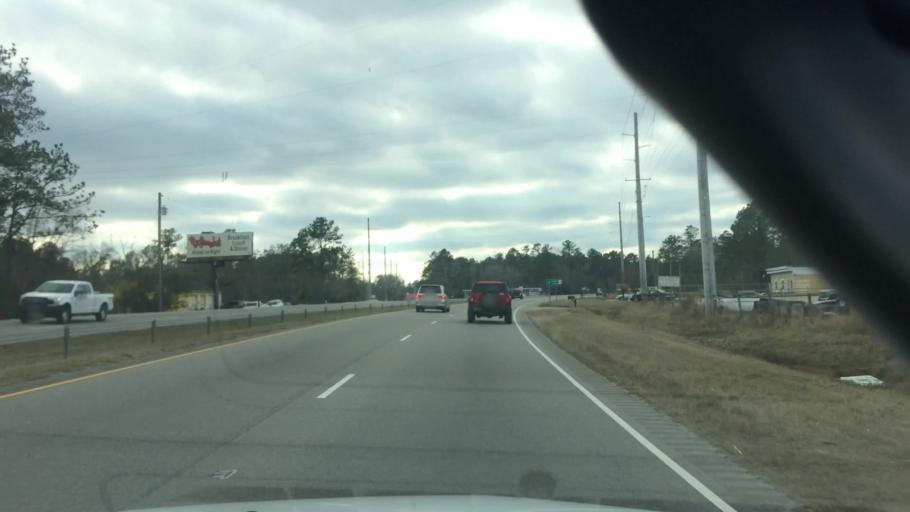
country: US
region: North Carolina
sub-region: Brunswick County
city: Bolivia
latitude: 34.0219
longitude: -78.2646
